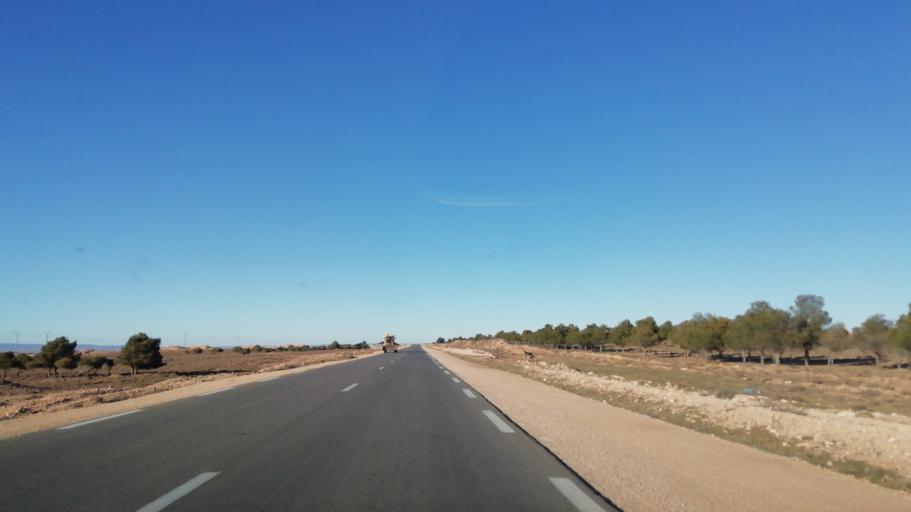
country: DZ
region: Tlemcen
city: Sebdou
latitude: 34.2726
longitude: -1.2585
